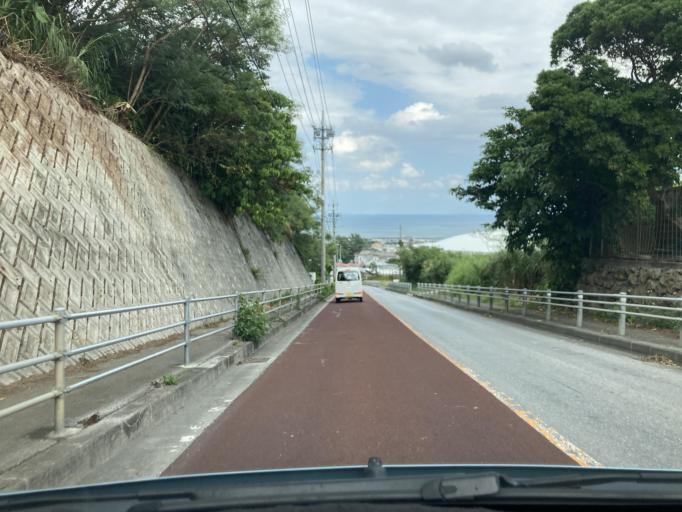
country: JP
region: Okinawa
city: Ginowan
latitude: 26.2515
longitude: 127.7794
